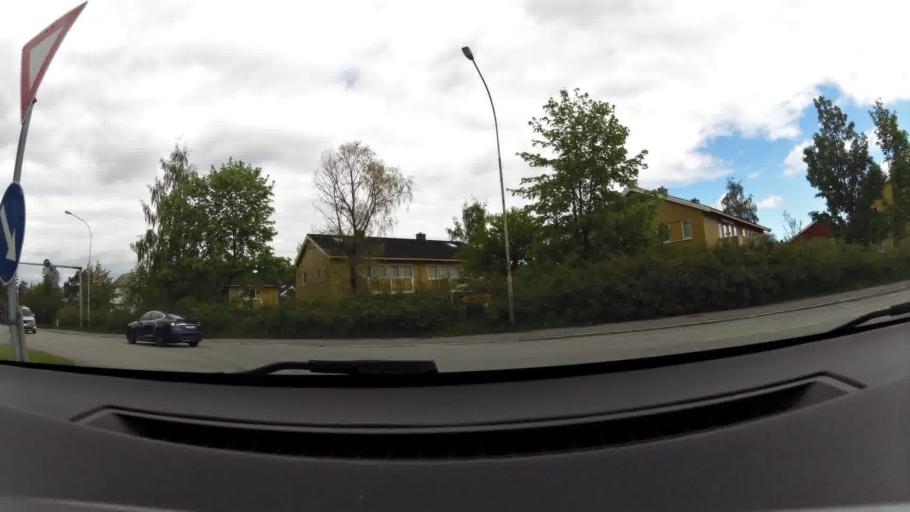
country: NO
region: Sor-Trondelag
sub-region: Trondheim
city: Trondheim
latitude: 63.4040
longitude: 10.4280
